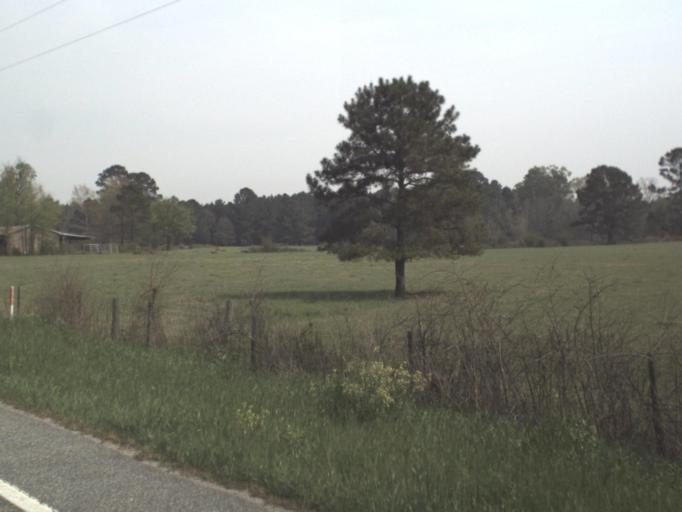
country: US
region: Florida
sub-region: Jackson County
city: Malone
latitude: 30.9761
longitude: -85.0234
